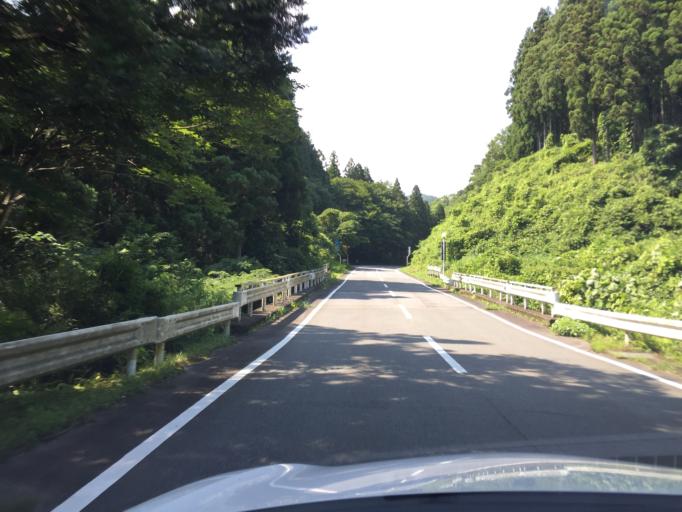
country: JP
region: Ibaraki
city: Kitaibaraki
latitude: 36.9411
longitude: 140.7187
